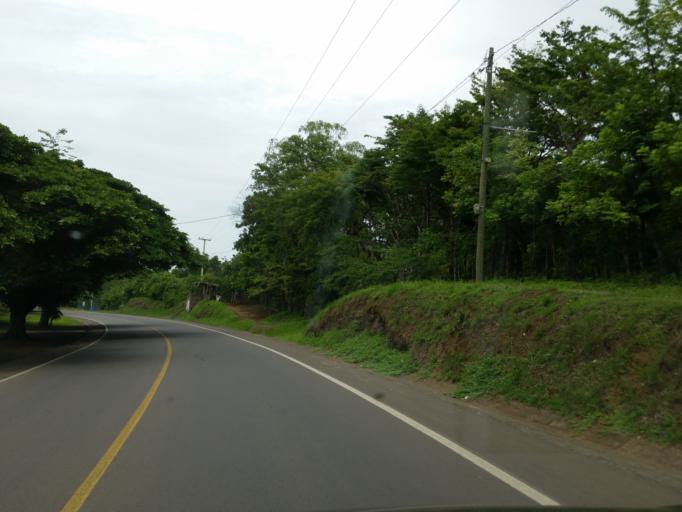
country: NI
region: Masaya
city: Masaya
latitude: 11.9719
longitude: -86.0703
